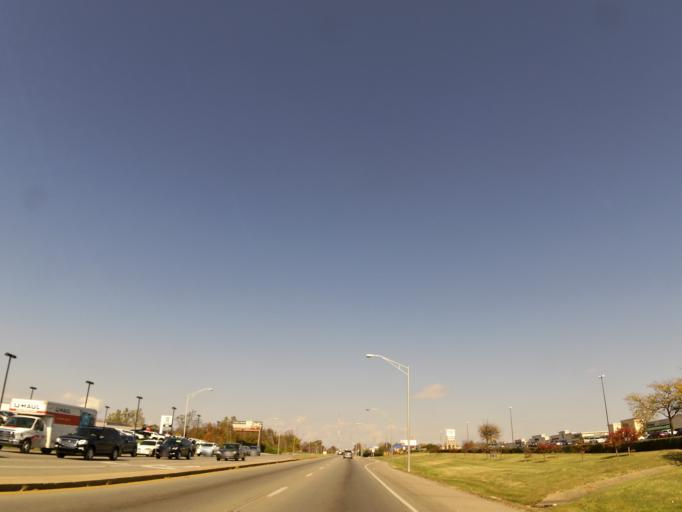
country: US
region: Kentucky
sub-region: Fayette County
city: Lexington-Fayette
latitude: 38.0184
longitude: -84.4562
